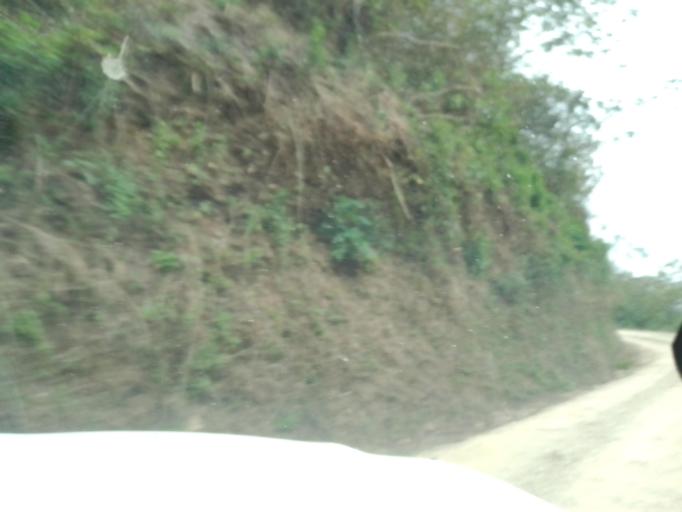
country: MX
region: Chiapas
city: Motozintla de Mendoza
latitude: 15.2197
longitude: -92.2215
